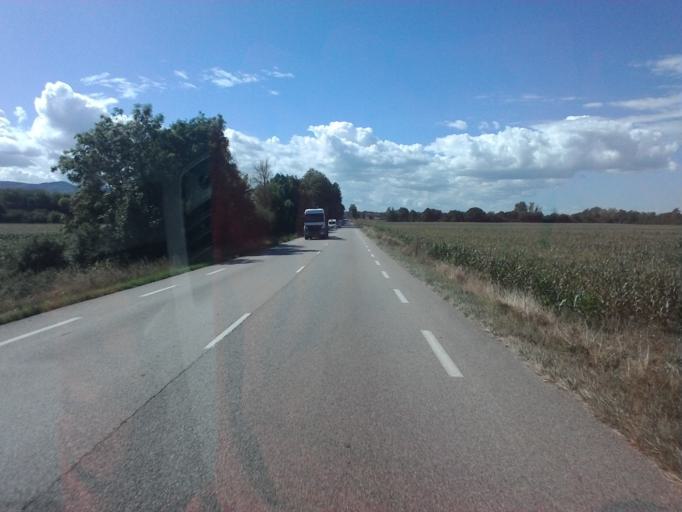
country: FR
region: Rhone-Alpes
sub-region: Departement de l'Ain
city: Ambronay
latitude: 46.0015
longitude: 5.3419
